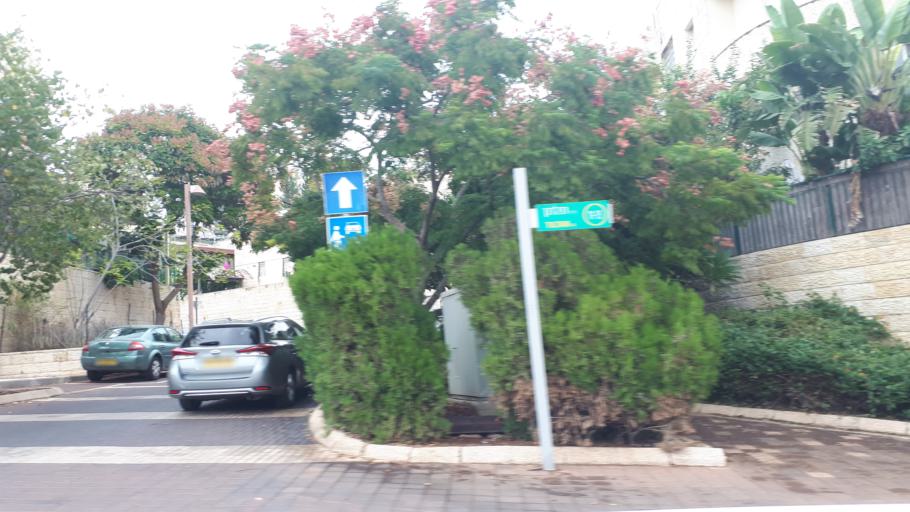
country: IL
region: Central District
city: Modiin
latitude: 31.9058
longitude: 35.0079
